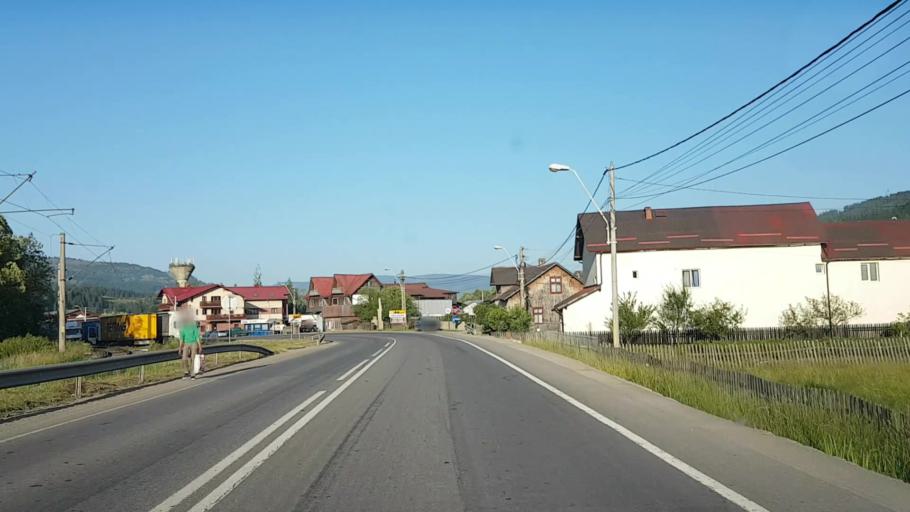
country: RO
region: Suceava
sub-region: Municipiul Vatra Dornei
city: Vatra Dornei
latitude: 47.3471
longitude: 25.3220
